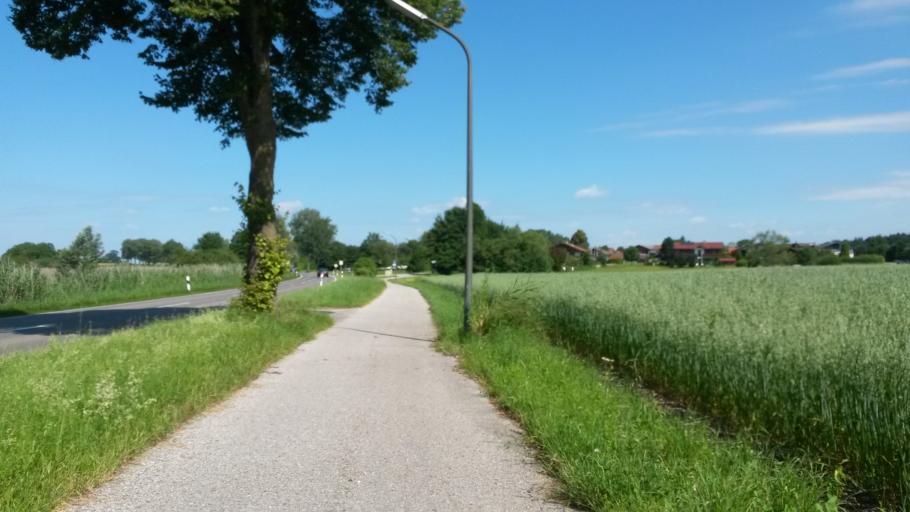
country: DE
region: Bavaria
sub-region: Upper Bavaria
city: Grabenstatt
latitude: 47.8533
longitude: 12.5397
